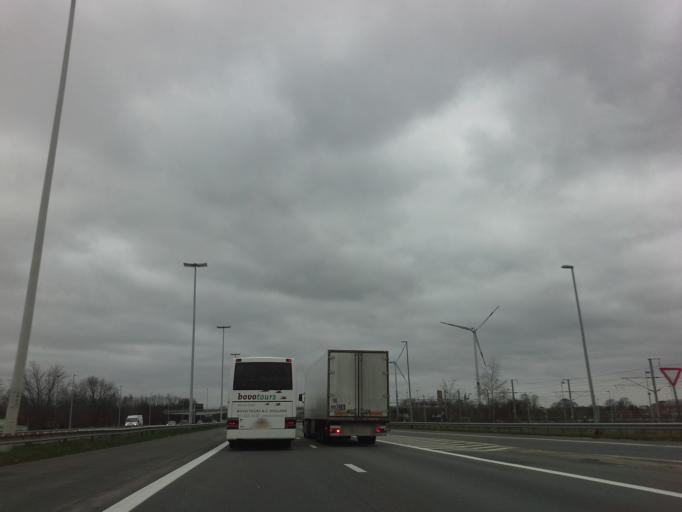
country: BE
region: Flanders
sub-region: Provincie Antwerpen
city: Brecht
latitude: 51.3567
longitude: 4.6334
